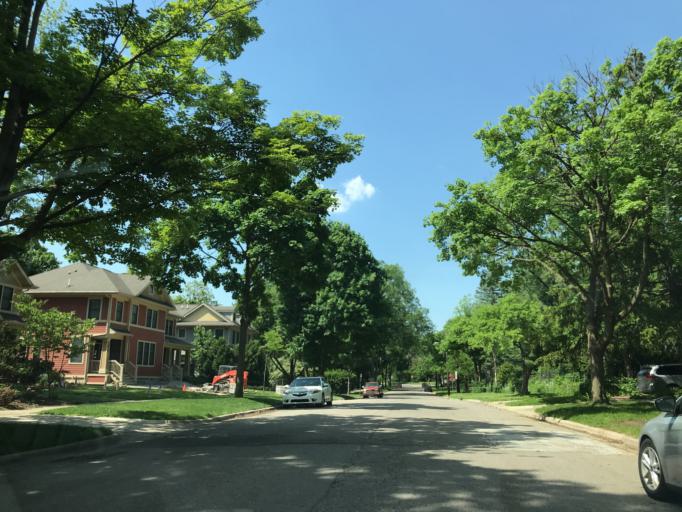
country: US
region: Michigan
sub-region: Washtenaw County
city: Ann Arbor
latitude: 42.2696
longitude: -83.7272
